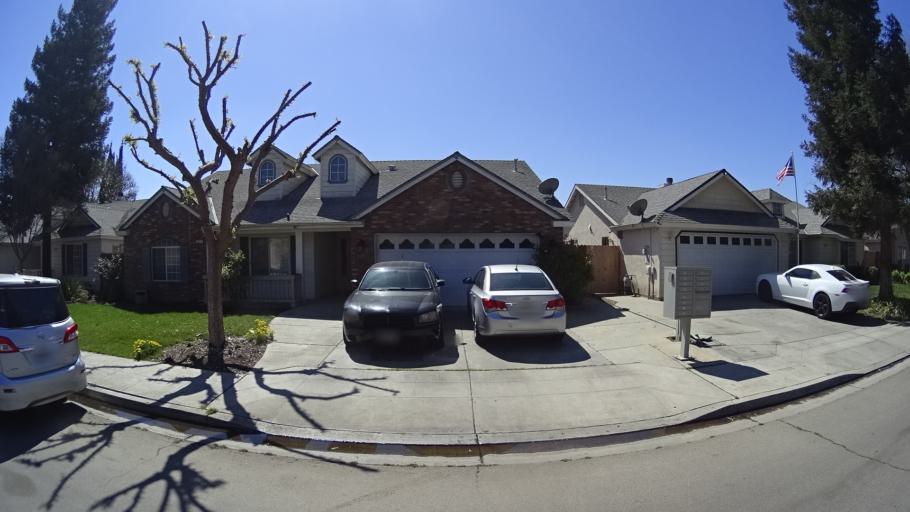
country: US
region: California
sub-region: Fresno County
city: West Park
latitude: 36.7830
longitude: -119.8856
